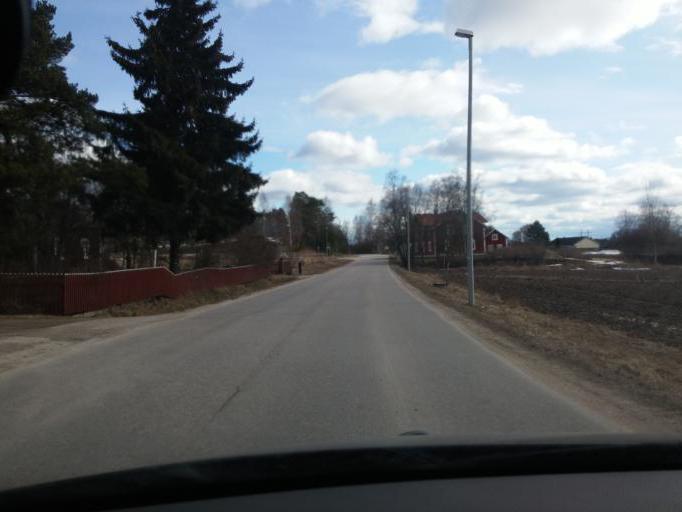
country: SE
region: Gaevleborg
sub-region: Ljusdals Kommun
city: Ljusdal
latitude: 61.8211
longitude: 16.1241
